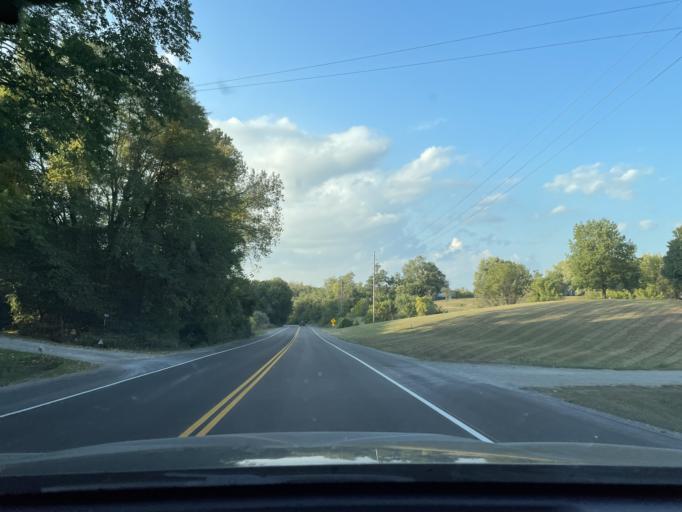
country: US
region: Missouri
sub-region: Andrew County
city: Country Club Village
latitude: 39.8517
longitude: -94.8702
